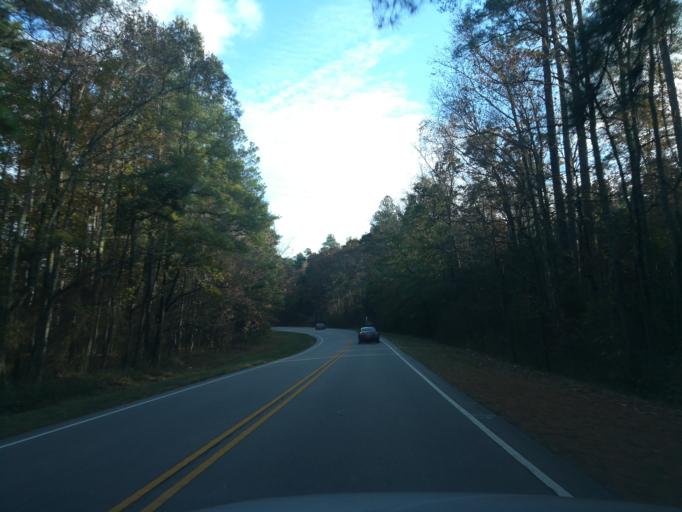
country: US
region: North Carolina
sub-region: Durham County
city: Durham
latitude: 36.0224
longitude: -78.9882
